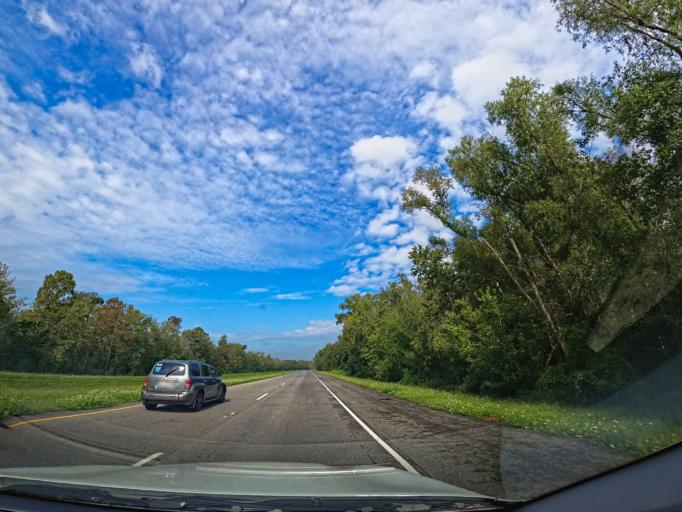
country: US
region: Louisiana
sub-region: Saint Mary Parish
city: Patterson
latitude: 29.7154
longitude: -91.4015
